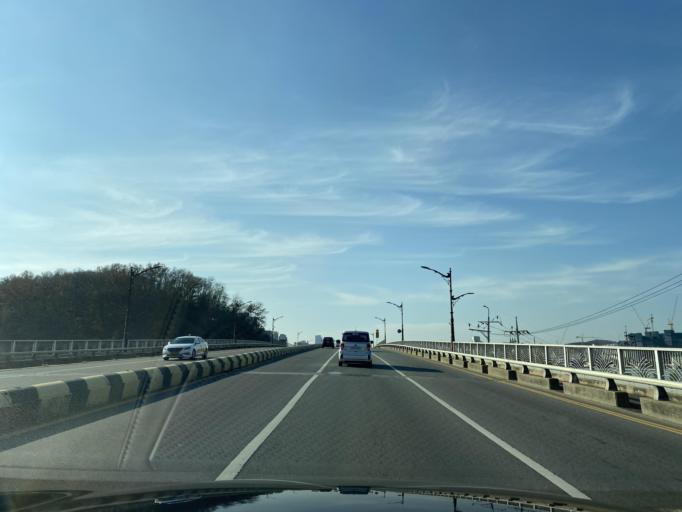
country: KR
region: Chungcheongnam-do
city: Cheonan
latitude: 36.7984
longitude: 127.1488
